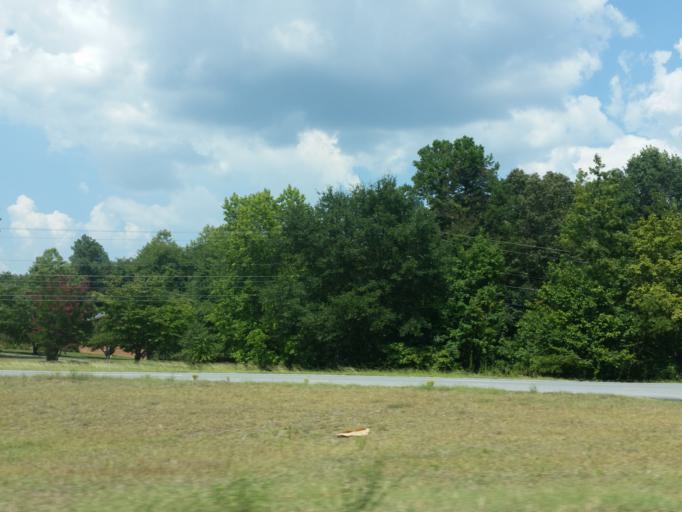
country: US
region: North Carolina
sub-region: Cleveland County
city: White Plains
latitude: 35.2469
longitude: -81.4279
